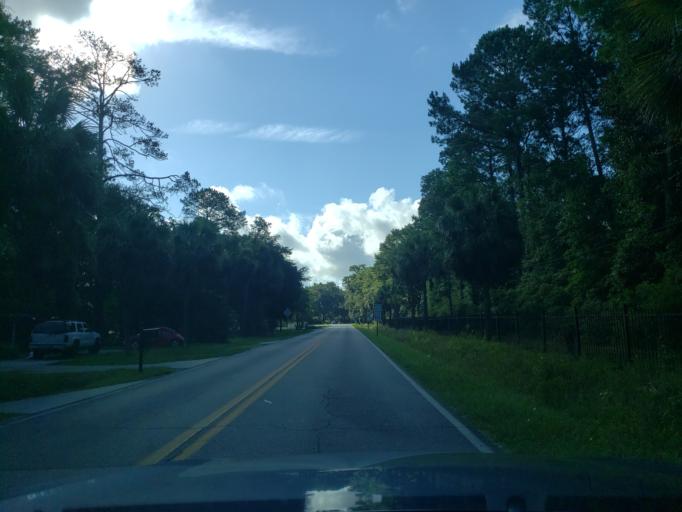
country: US
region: Georgia
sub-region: Chatham County
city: Isle of Hope
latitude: 31.9797
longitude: -81.0671
